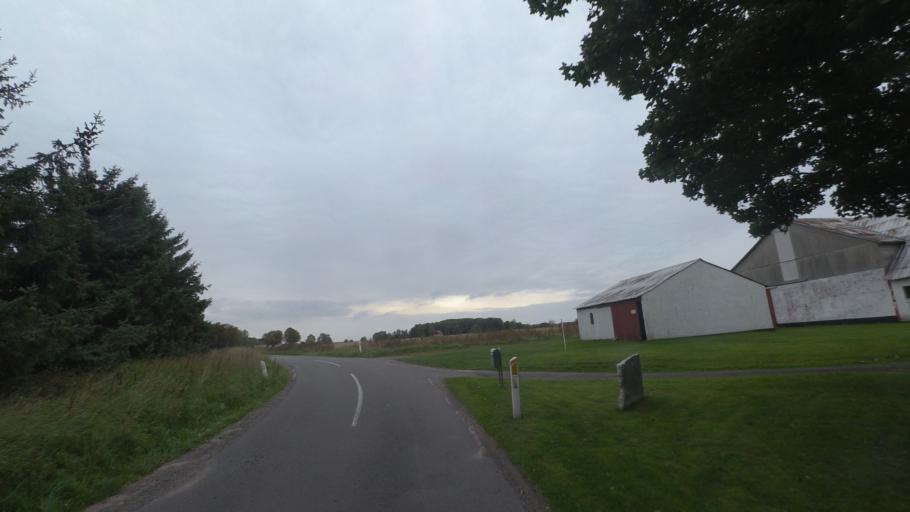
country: DK
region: Capital Region
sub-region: Bornholm Kommune
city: Akirkeby
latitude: 55.0053
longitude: 14.9928
